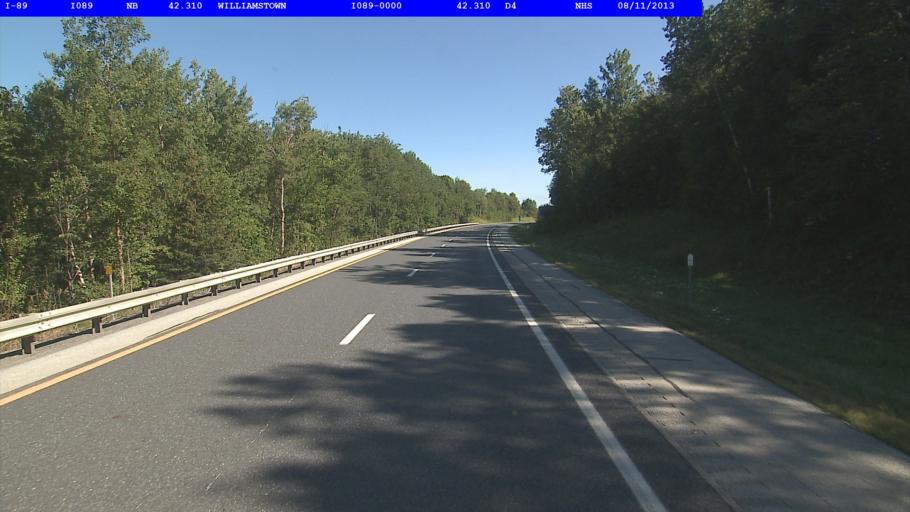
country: US
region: Vermont
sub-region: Washington County
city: Northfield
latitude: 44.1063
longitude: -72.6115
